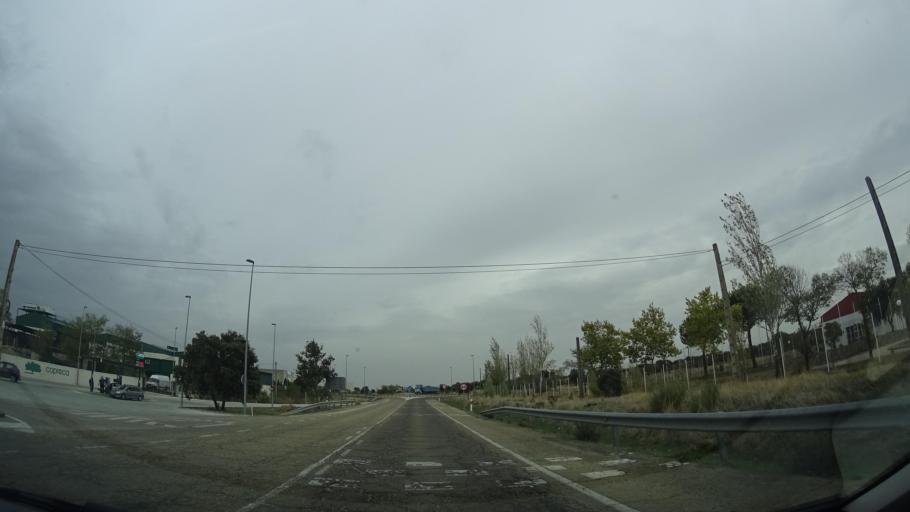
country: ES
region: Extremadura
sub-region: Provincia de Caceres
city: Trujillo
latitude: 39.4812
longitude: -5.8540
